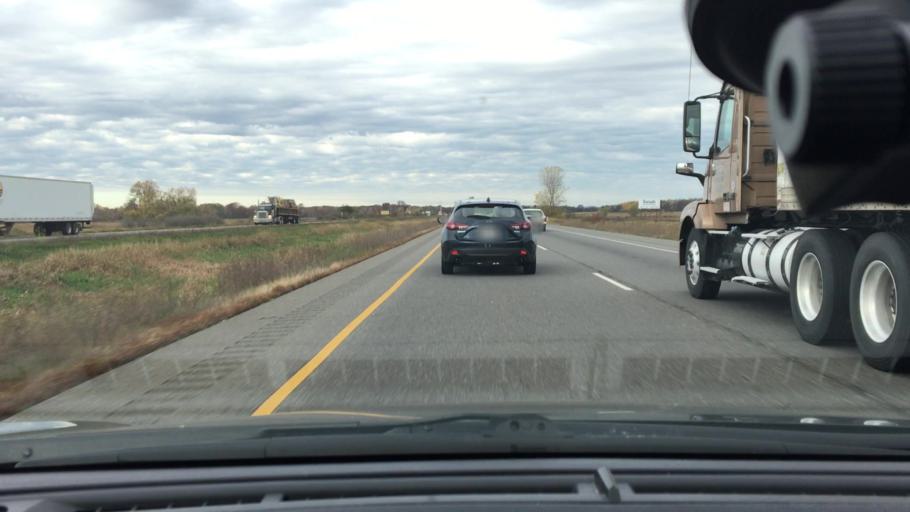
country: US
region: Wisconsin
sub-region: Monroe County
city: Tomah
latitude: 43.9742
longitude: -90.4093
